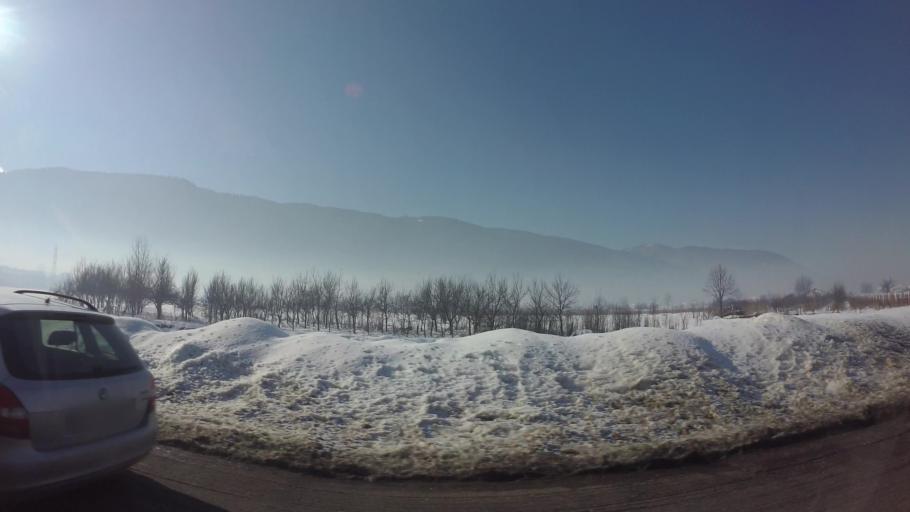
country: BA
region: Federation of Bosnia and Herzegovina
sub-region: Kanton Sarajevo
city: Sarajevo
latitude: 43.8045
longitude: 18.3119
